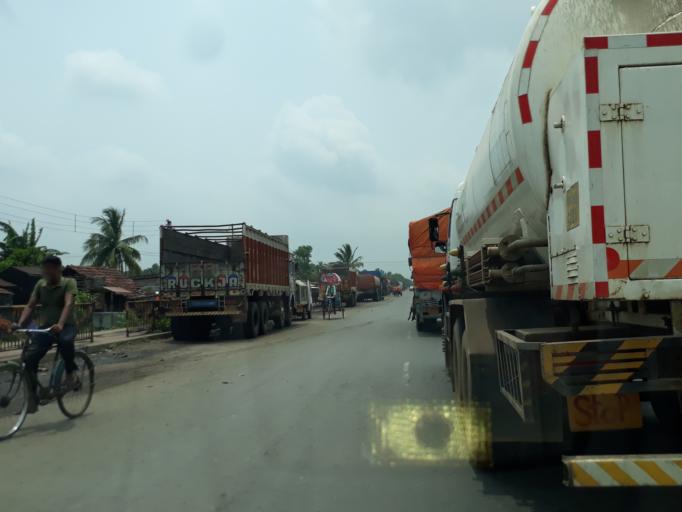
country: IN
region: West Bengal
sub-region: Purba Medinipur
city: Mahishadal
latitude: 22.1411
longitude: 87.9780
